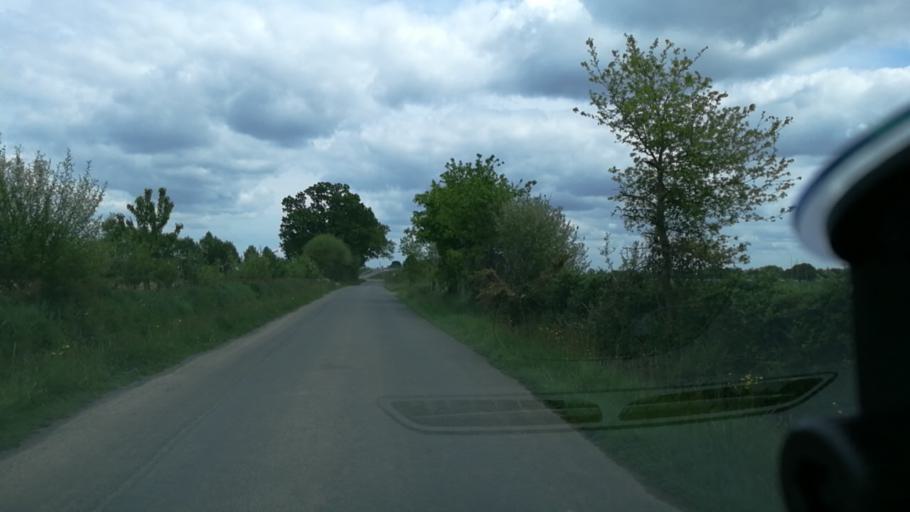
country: FR
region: Brittany
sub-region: Departement d'Ille-et-Vilaine
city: Retiers
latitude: 47.8926
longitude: -1.3758
